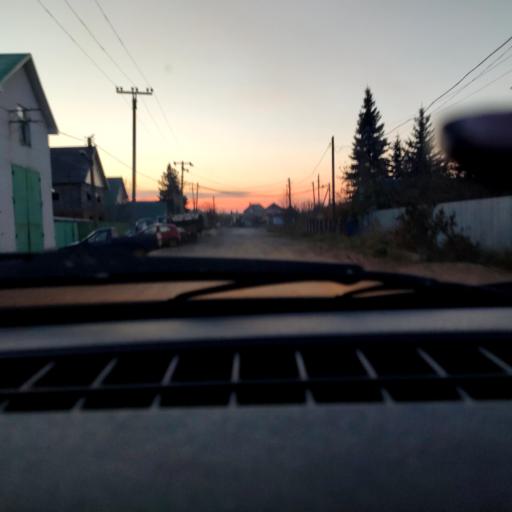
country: RU
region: Bashkortostan
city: Iglino
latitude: 54.8352
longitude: 56.1828
